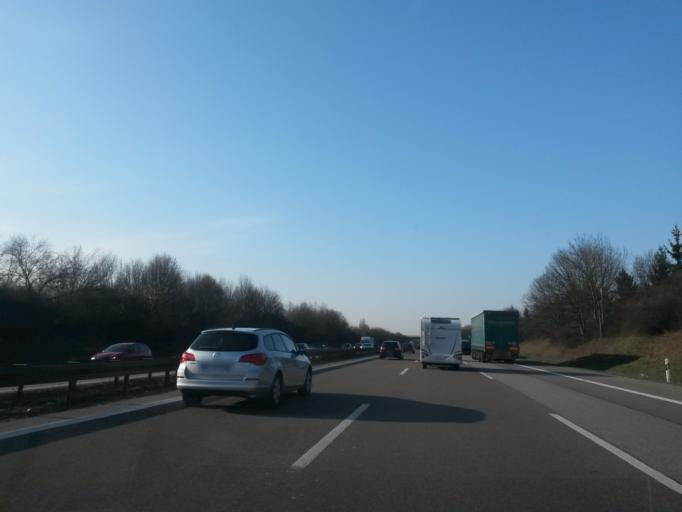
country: DE
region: Bavaria
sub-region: Upper Bavaria
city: Manching
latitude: 48.7333
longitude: 11.4705
